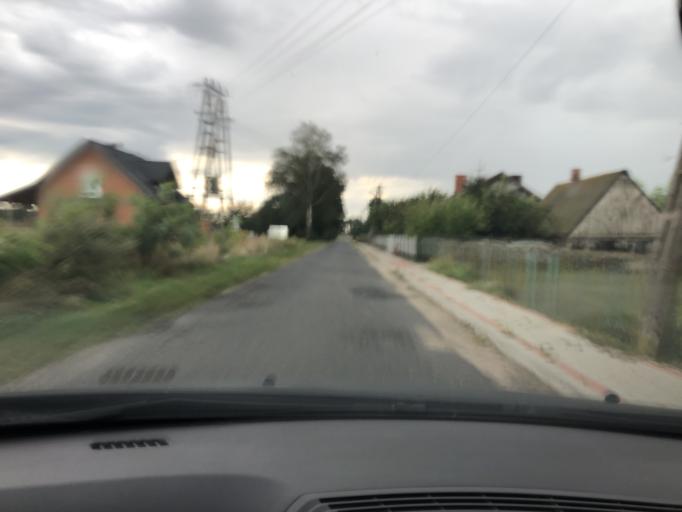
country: PL
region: Lodz Voivodeship
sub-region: Powiat wieruszowski
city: Czastary
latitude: 51.2404
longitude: 18.2917
